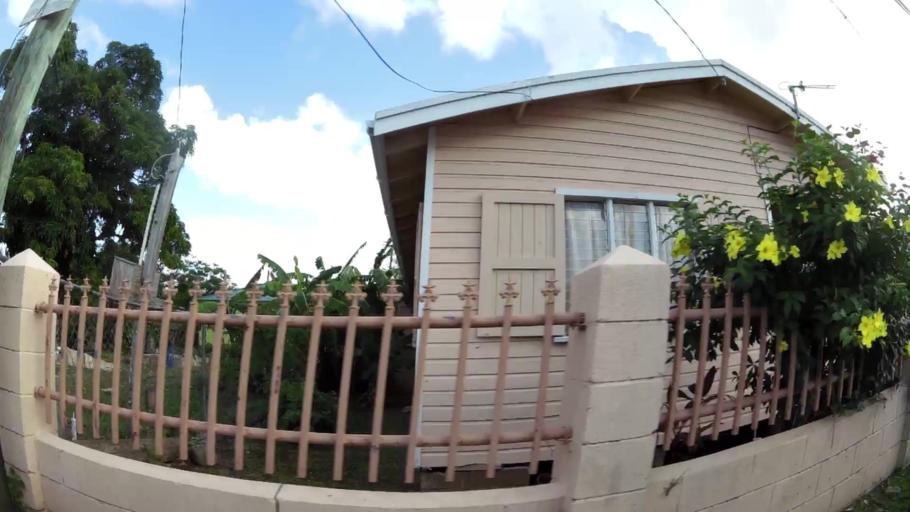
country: AG
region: Saint John
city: Saint John's
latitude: 17.1078
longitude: -61.8383
